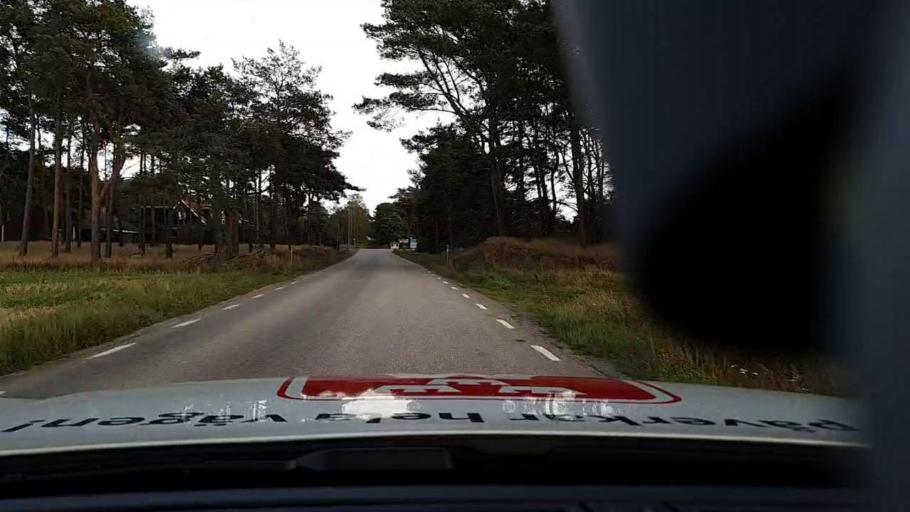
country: SE
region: Blekinge
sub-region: Solvesborgs Kommun
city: Soelvesborg
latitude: 56.0251
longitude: 14.7165
